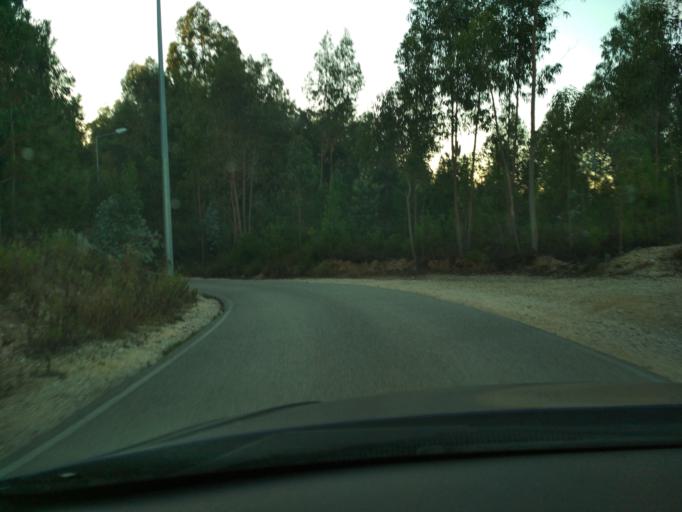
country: PT
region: Coimbra
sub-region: Coimbra
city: Coimbra
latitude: 40.1811
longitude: -8.4716
